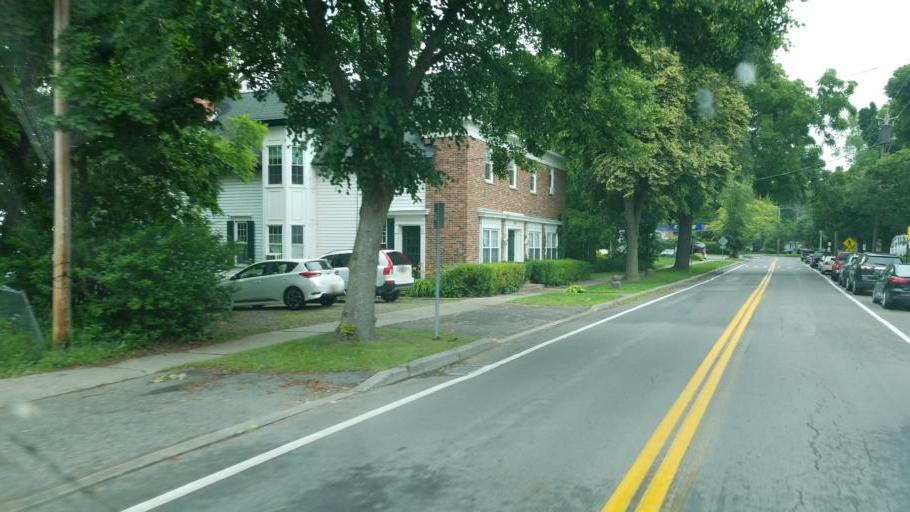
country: US
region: New York
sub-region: Niagara County
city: Youngstown
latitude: 43.2509
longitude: -79.0499
